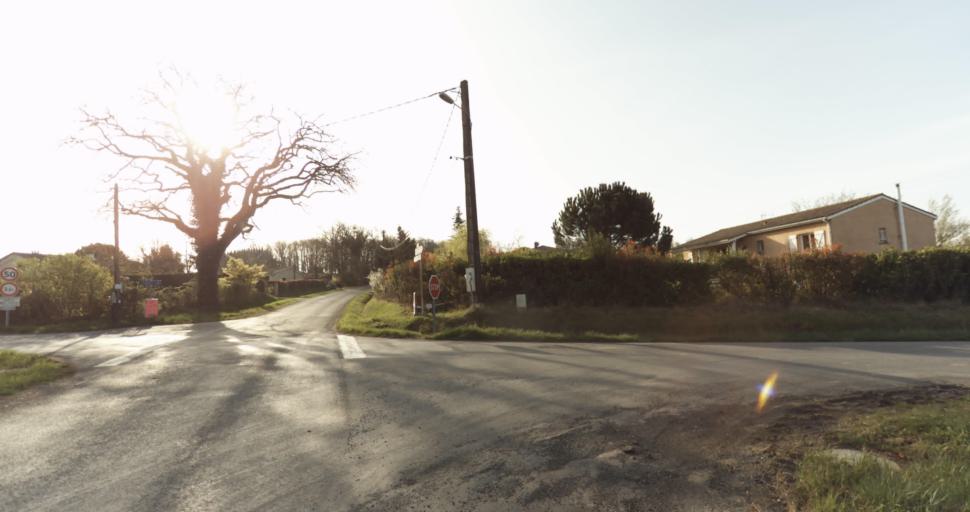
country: FR
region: Midi-Pyrenees
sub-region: Departement du Tarn
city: Saint-Sulpice-la-Pointe
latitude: 43.7312
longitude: 1.6984
